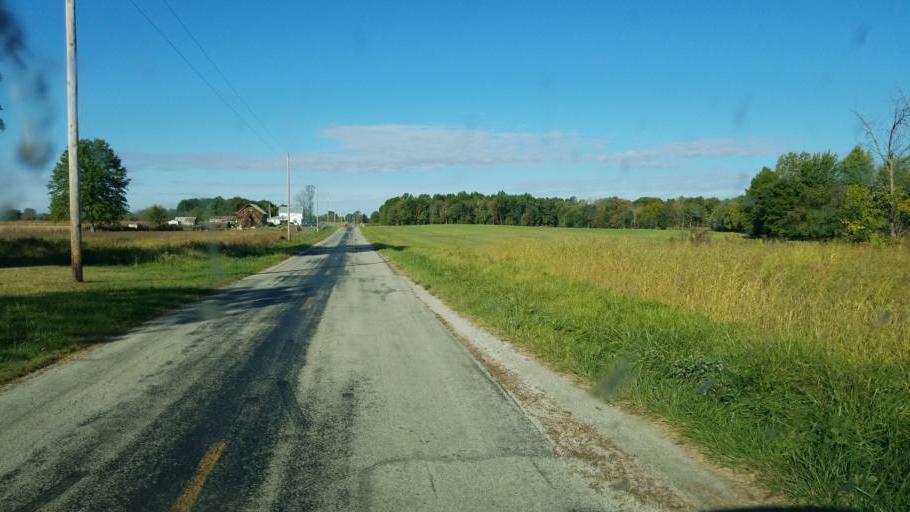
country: US
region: Ohio
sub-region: Crawford County
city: Bucyrus
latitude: 40.6897
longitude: -82.9249
